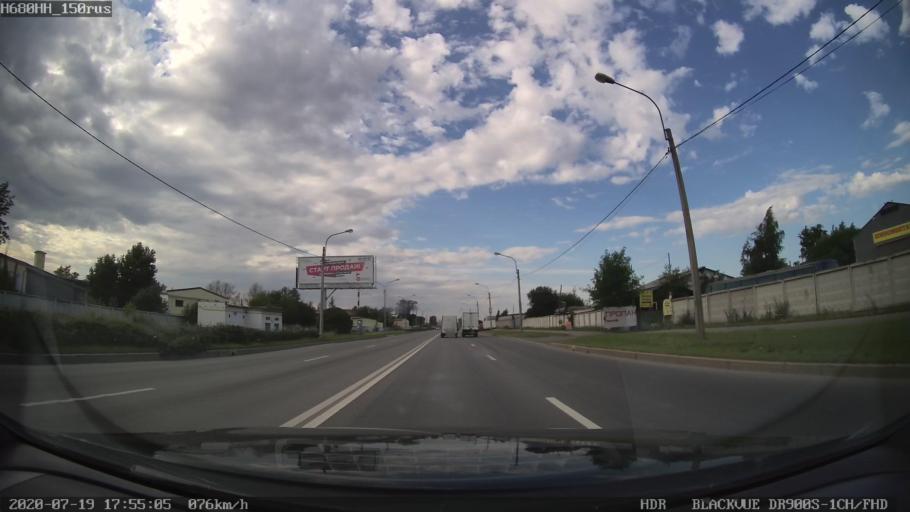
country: RU
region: St.-Petersburg
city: Admiralteisky
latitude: 59.8915
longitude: 30.3019
